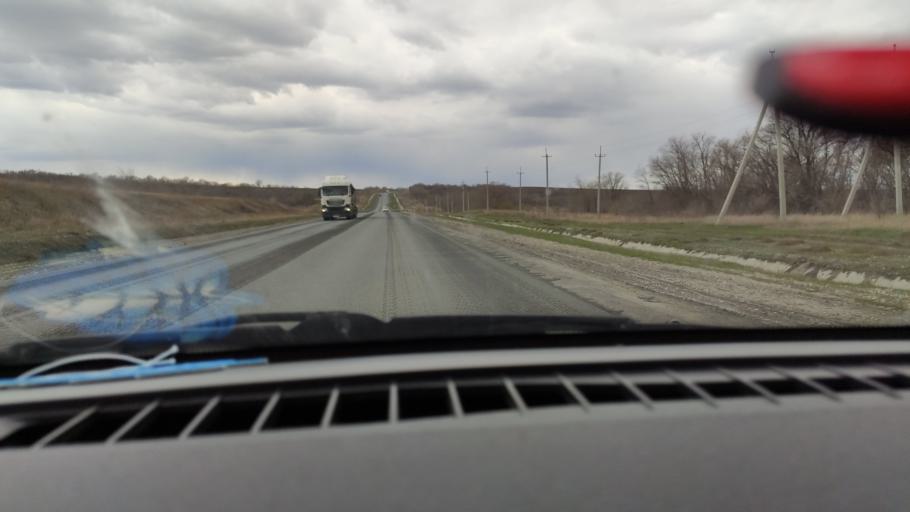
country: RU
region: Saratov
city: Shumeyka
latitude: 51.7823
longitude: 46.1285
